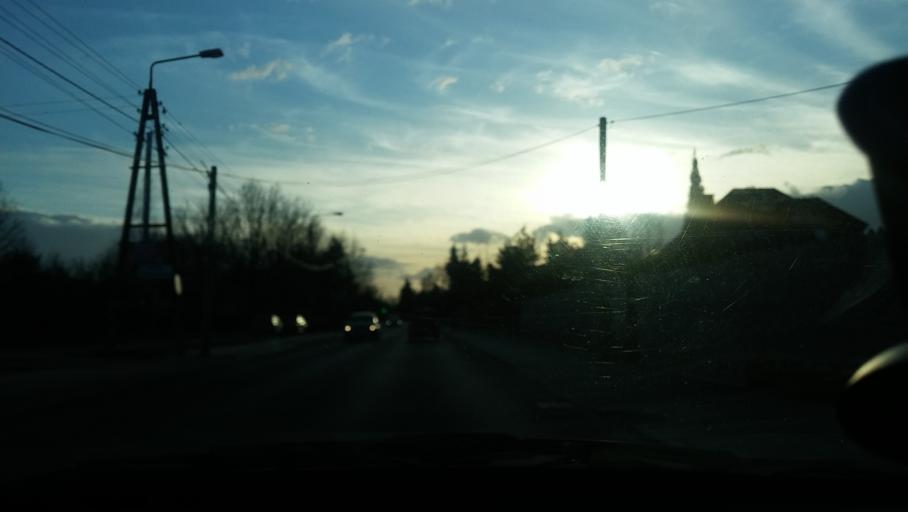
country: PL
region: Masovian Voivodeship
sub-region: Warszawa
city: Wawer
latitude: 52.2000
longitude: 21.1468
